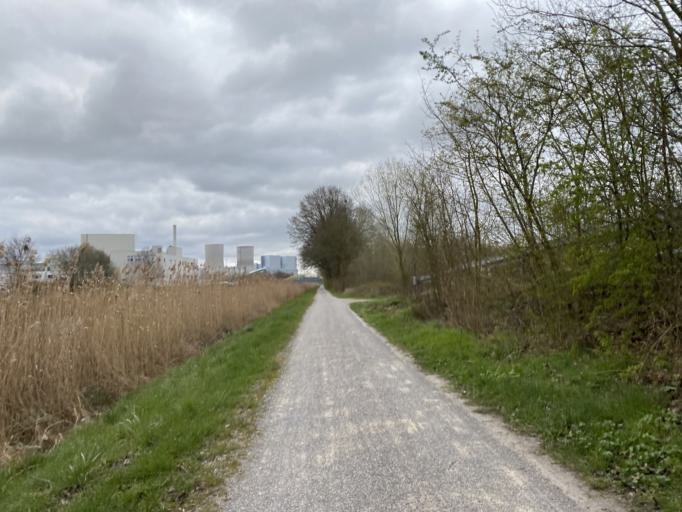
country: DE
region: North Rhine-Westphalia
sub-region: Regierungsbezirk Arnsberg
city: Welver
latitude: 51.6838
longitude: 7.9456
